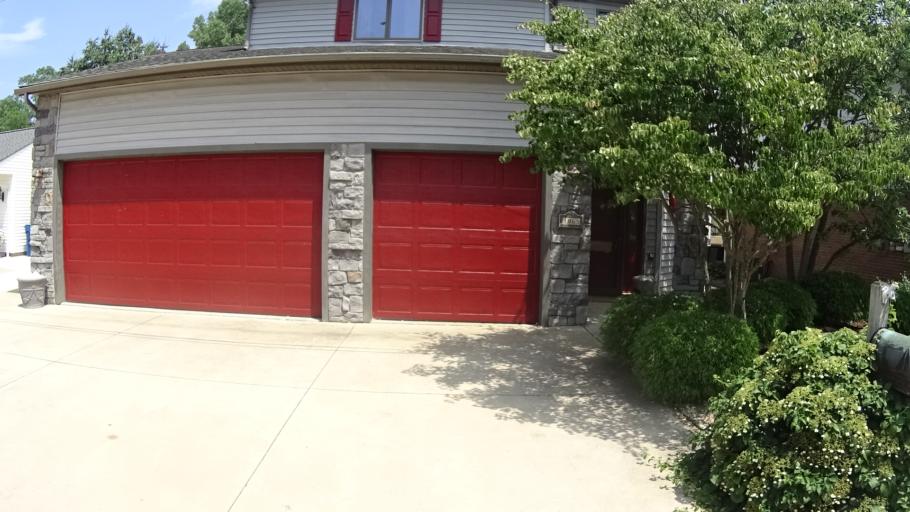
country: US
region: Ohio
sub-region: Lorain County
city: Vermilion
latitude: 41.4149
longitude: -82.3518
